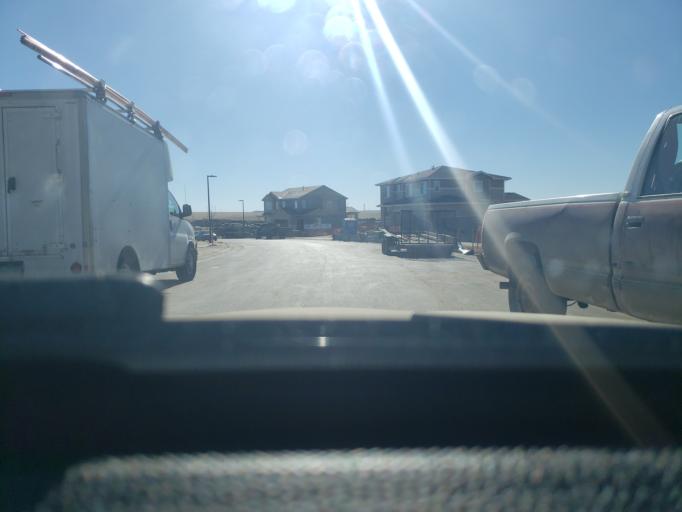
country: US
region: Colorado
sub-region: Adams County
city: Aurora
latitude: 39.7723
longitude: -104.7036
